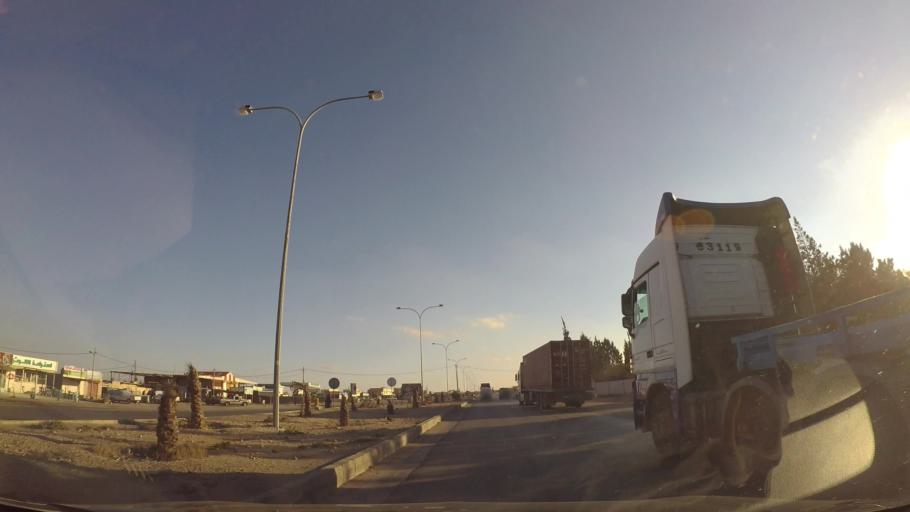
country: JO
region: Tafielah
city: Busayra
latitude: 30.5964
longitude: 35.8039
